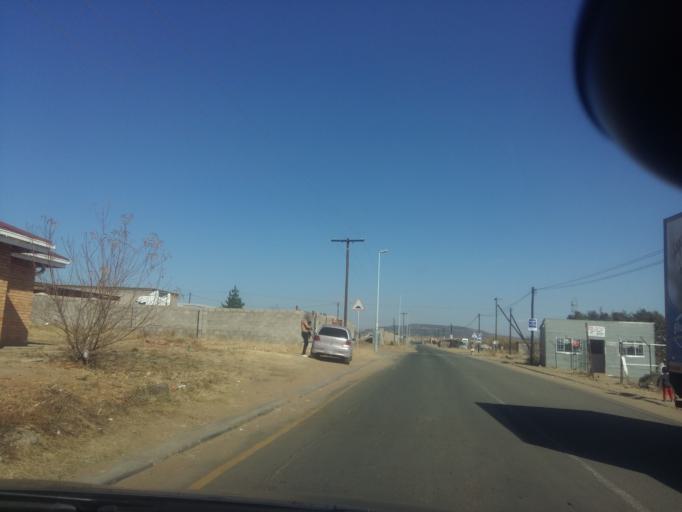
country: LS
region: Maseru
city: Maseru
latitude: -29.3399
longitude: 27.4428
